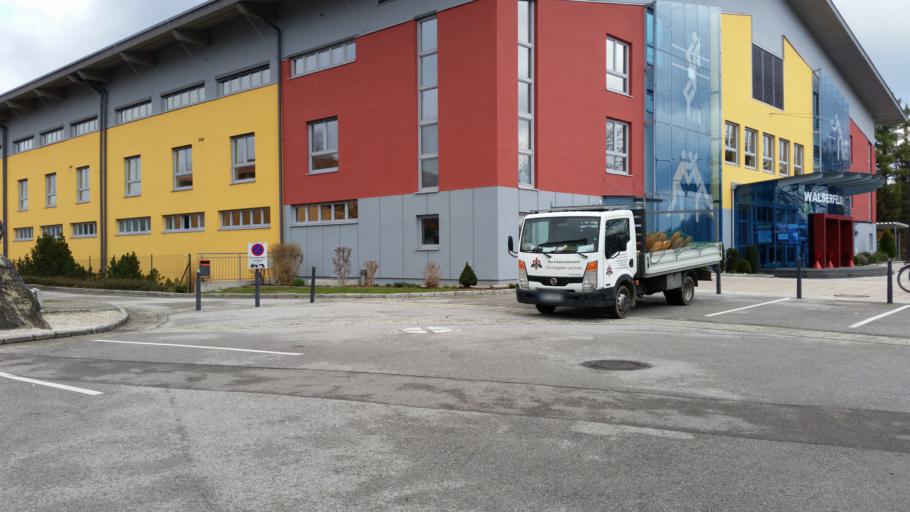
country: DE
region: Bavaria
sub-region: Upper Bavaria
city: Ainring
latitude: 47.7952
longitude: 12.9823
